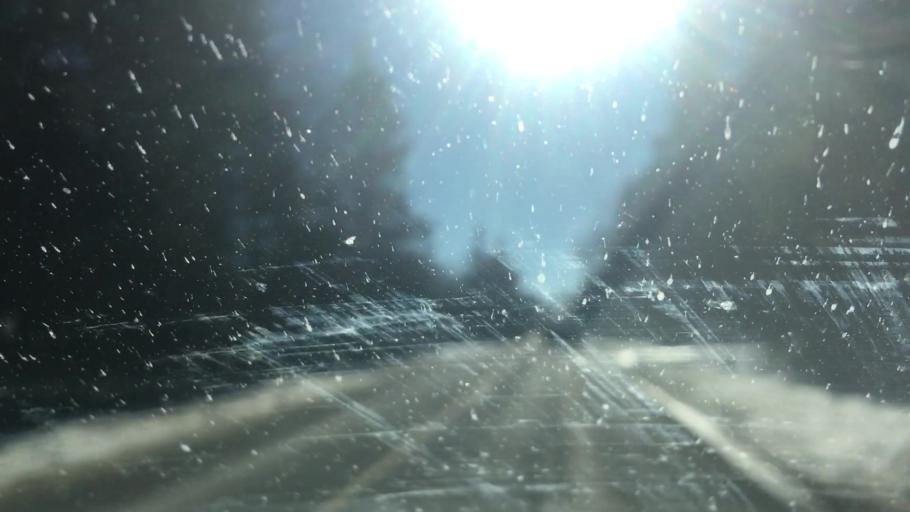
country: US
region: Maine
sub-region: Hancock County
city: Sedgwick
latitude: 44.3942
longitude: -68.6400
